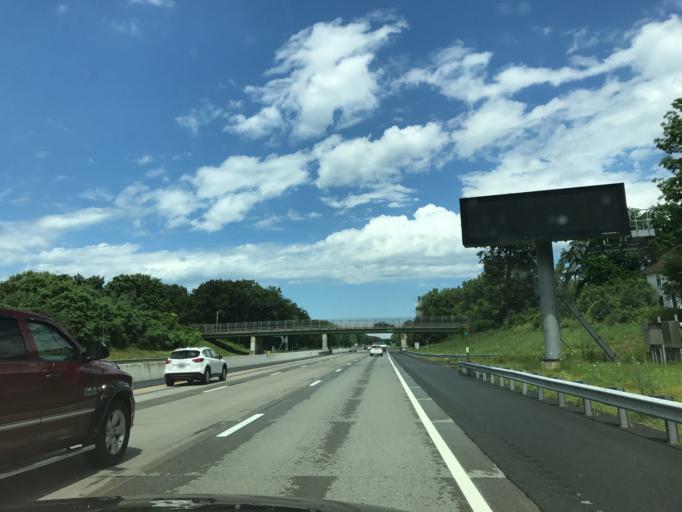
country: US
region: New York
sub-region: Albany County
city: McKownville
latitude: 42.6643
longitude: -73.8311
